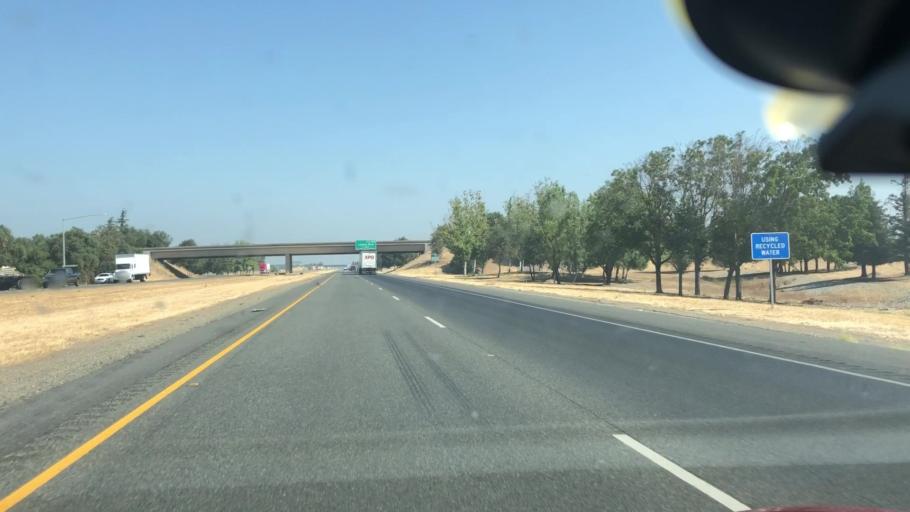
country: US
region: California
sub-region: Sacramento County
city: Laguna
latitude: 38.4069
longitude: -121.4832
